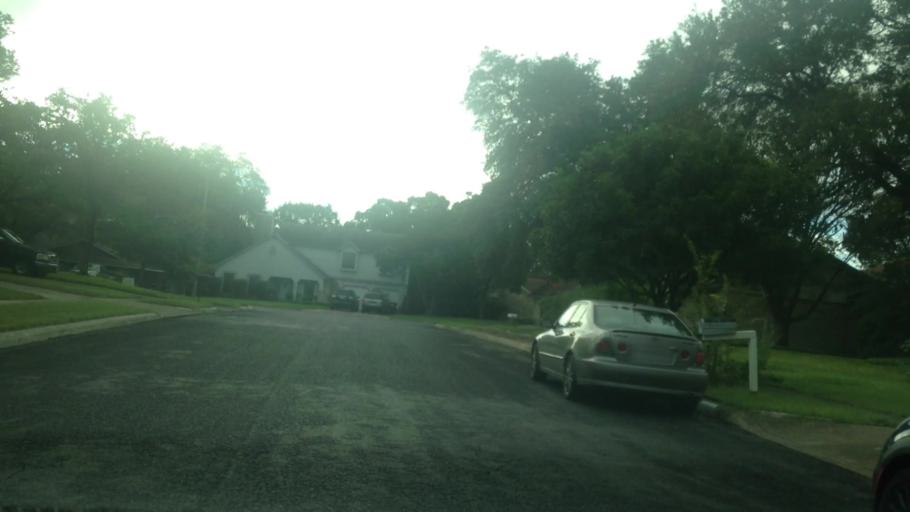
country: US
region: Texas
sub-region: Bexar County
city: Live Oak
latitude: 29.5899
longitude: -98.3745
